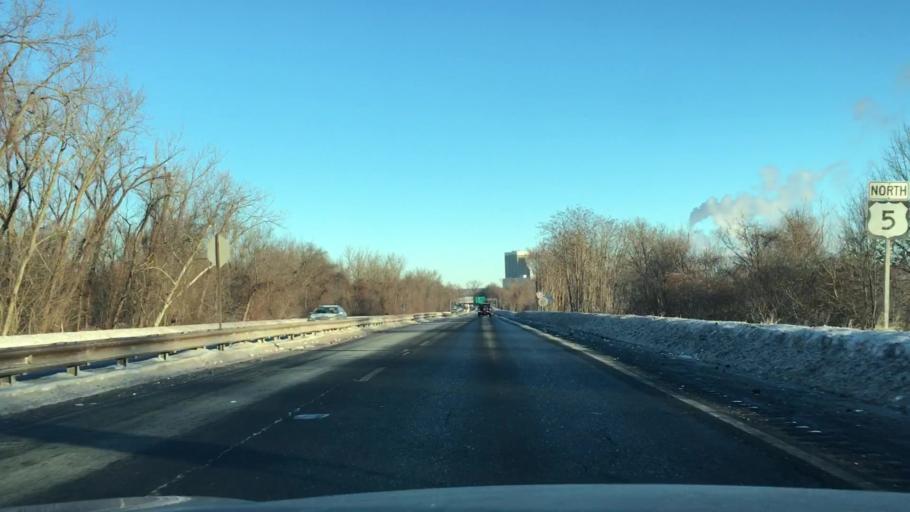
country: US
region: Massachusetts
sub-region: Hampden County
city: Springfield
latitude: 42.0850
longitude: -72.5916
